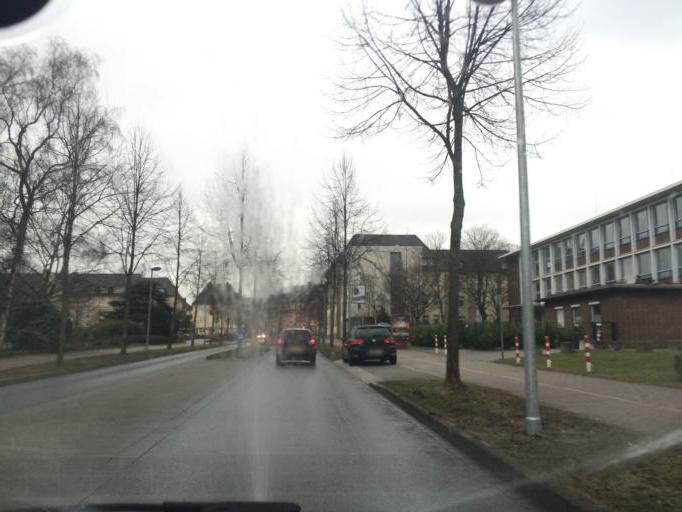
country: DE
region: North Rhine-Westphalia
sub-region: Regierungsbezirk Munster
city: Gladbeck
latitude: 51.5699
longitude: 6.9863
